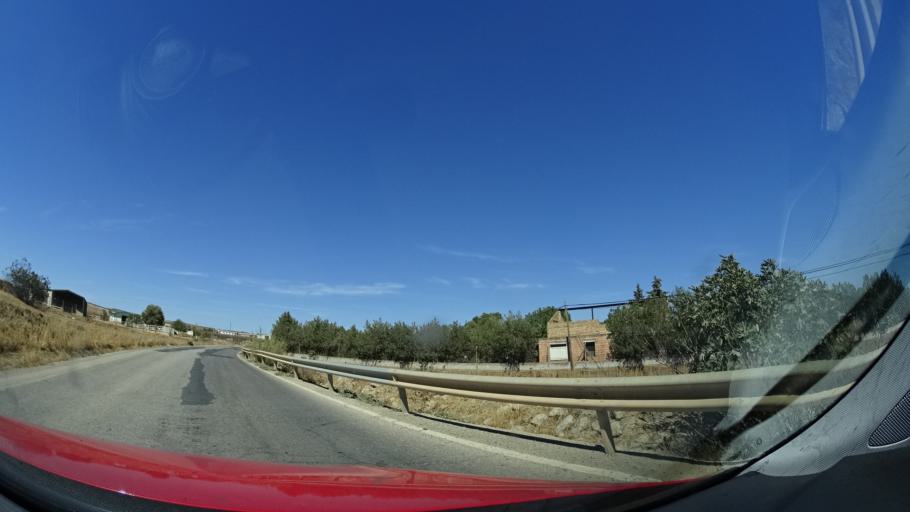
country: ES
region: Andalusia
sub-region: Provincia de Malaga
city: Campillos
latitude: 37.0572
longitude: -4.8639
